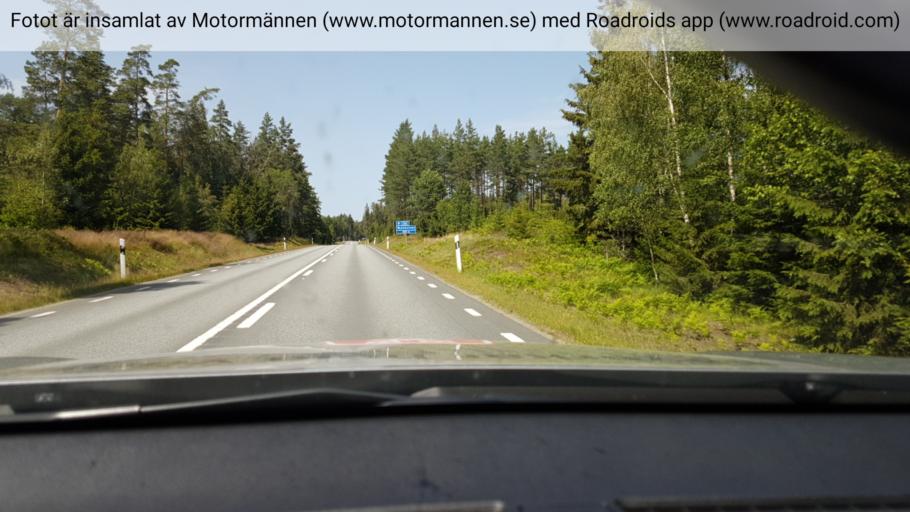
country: SE
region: Joenkoeping
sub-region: Nassjo Kommun
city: Bodafors
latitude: 57.5186
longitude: 14.7854
